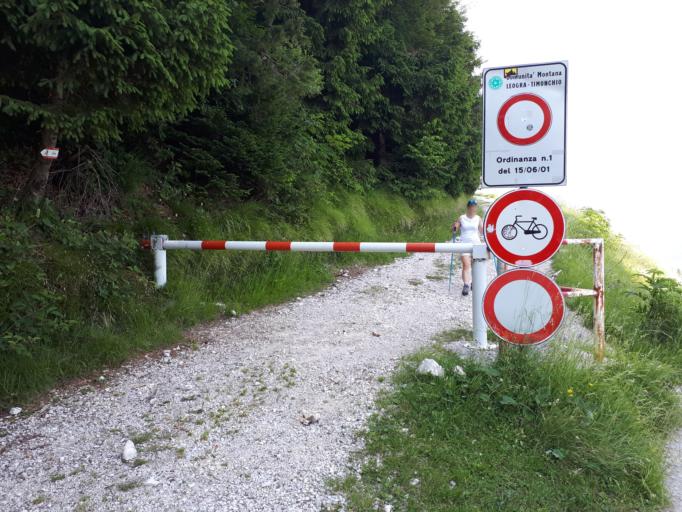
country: IT
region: Veneto
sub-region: Provincia di Vicenza
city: Posina
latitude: 45.7856
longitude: 11.2248
